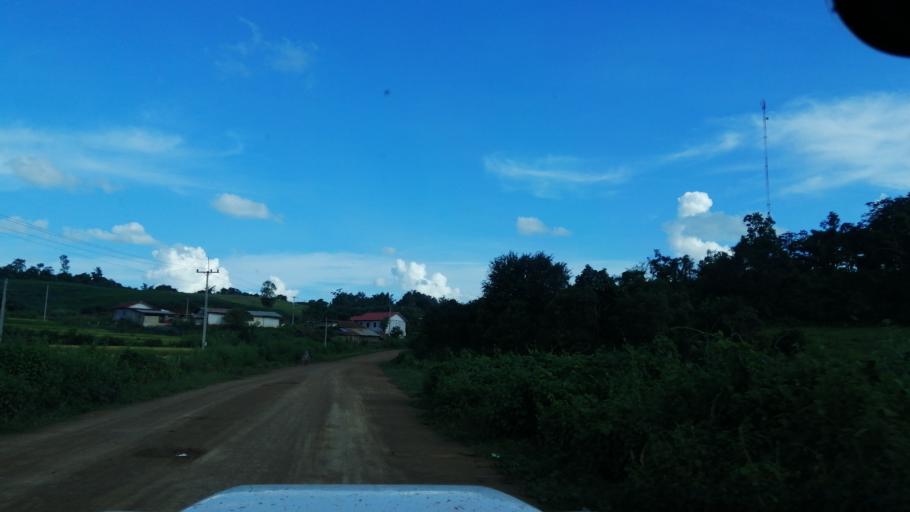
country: LA
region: Xiagnabouli
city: Muang Kenthao
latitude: 17.8468
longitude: 101.2446
